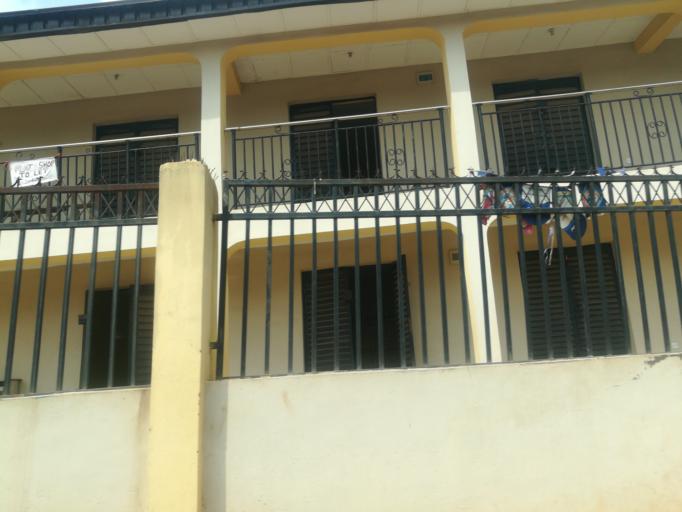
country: NG
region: Oyo
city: Ibadan
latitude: 7.4150
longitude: 3.9531
